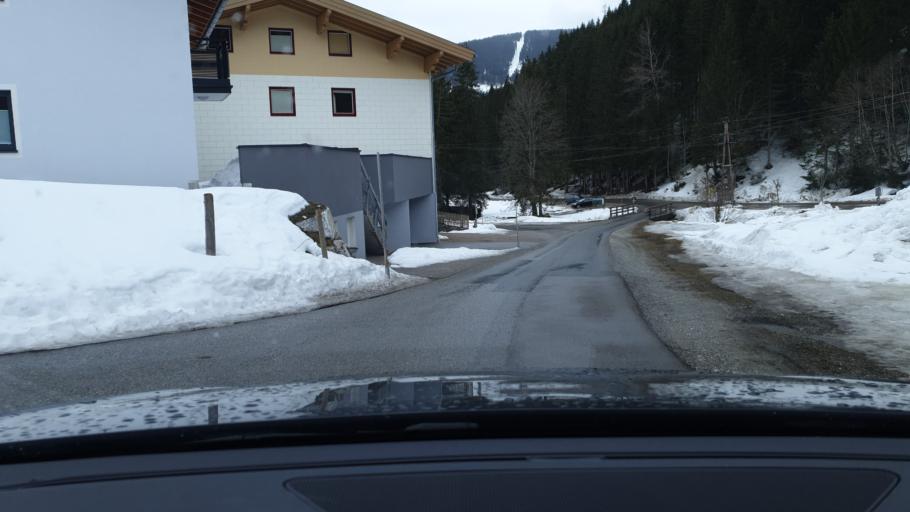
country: AT
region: Salzburg
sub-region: Politischer Bezirk Sankt Johann im Pongau
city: Filzmoos
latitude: 47.4440
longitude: 13.5196
